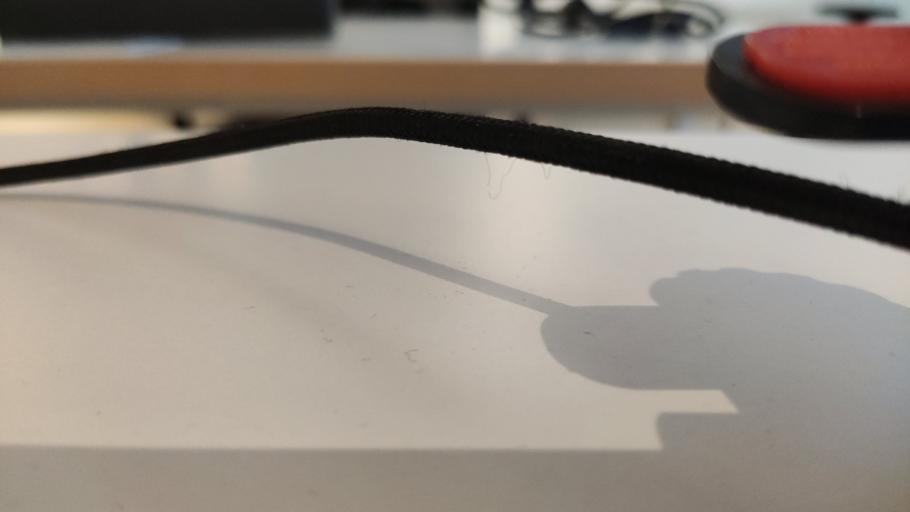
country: RU
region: Moskovskaya
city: Ruza
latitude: 55.8040
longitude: 36.2915
